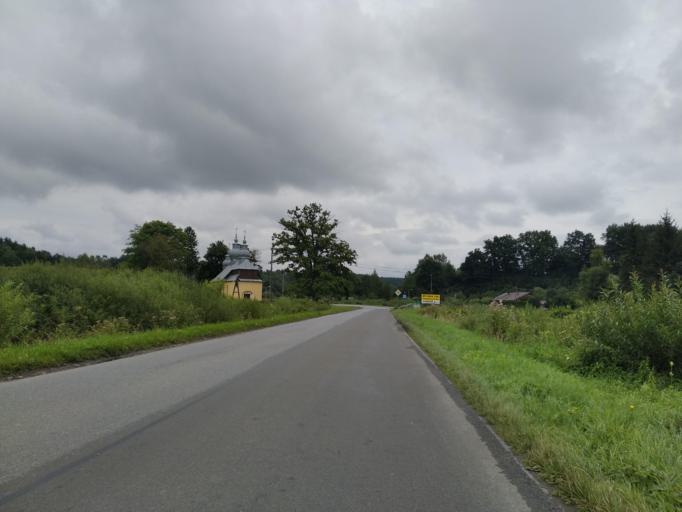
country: PL
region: Subcarpathian Voivodeship
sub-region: Powiat przemyski
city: Bircza
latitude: 49.6808
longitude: 22.4076
